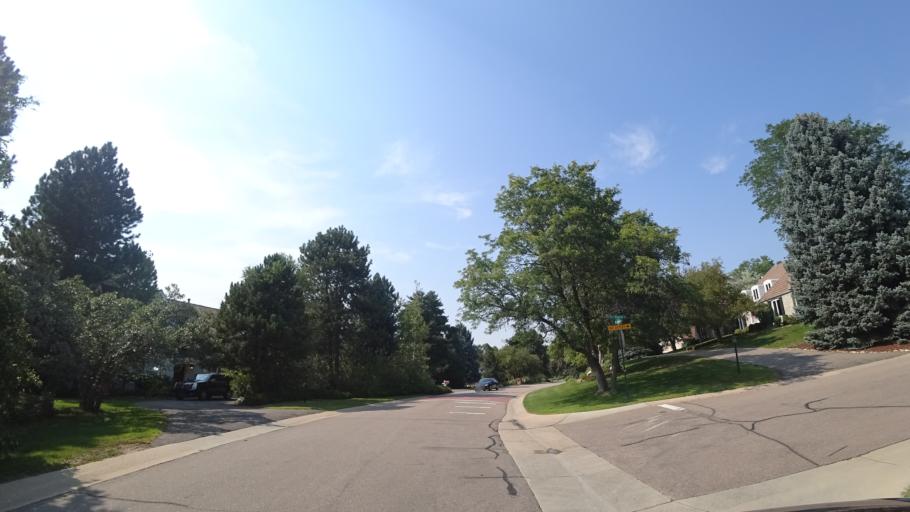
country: US
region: Colorado
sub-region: Arapahoe County
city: Greenwood Village
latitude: 39.6104
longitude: -104.9730
